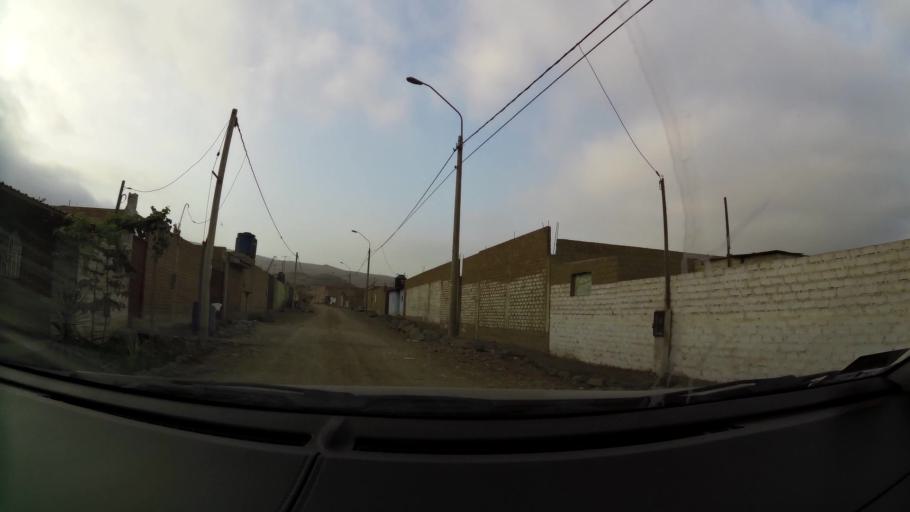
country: PE
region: Lima
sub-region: Lima
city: Santa Rosa
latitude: -11.7362
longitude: -77.1373
